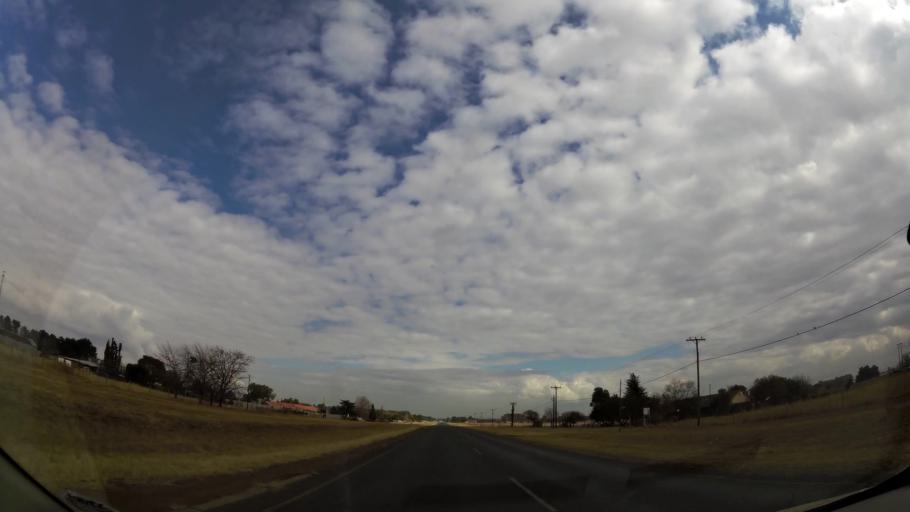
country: ZA
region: Gauteng
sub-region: Sedibeng District Municipality
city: Meyerton
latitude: -26.6394
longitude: 28.0504
